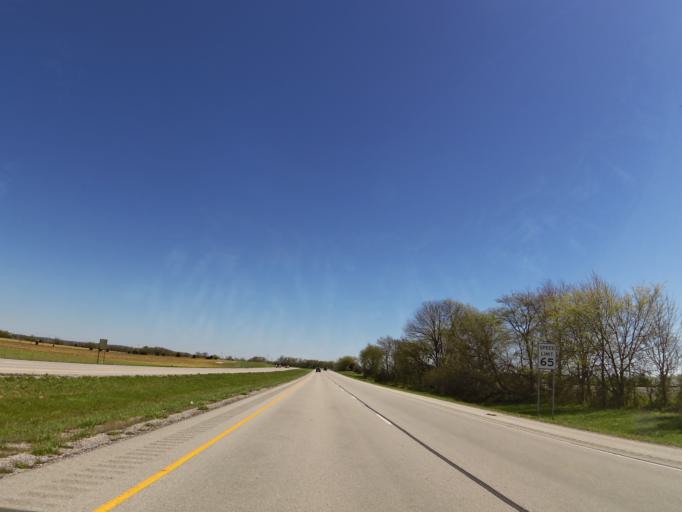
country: US
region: Kentucky
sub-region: Logan County
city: Auburn
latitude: 36.8943
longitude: -86.6033
